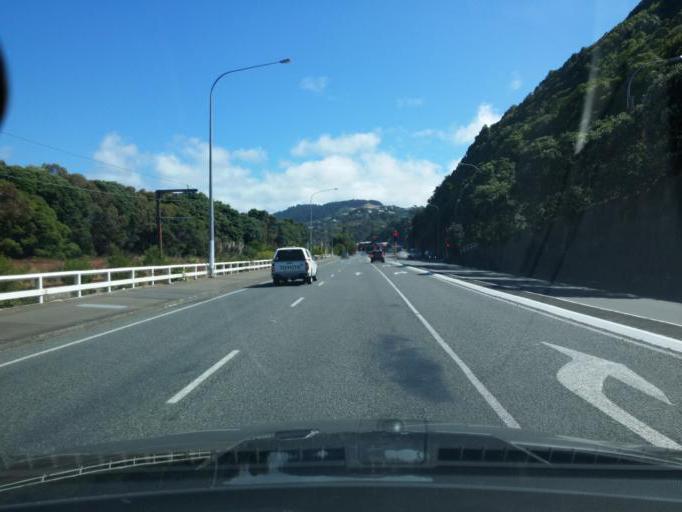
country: NZ
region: Wellington
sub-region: Wellington City
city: Wellington
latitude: -41.2540
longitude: 174.8014
